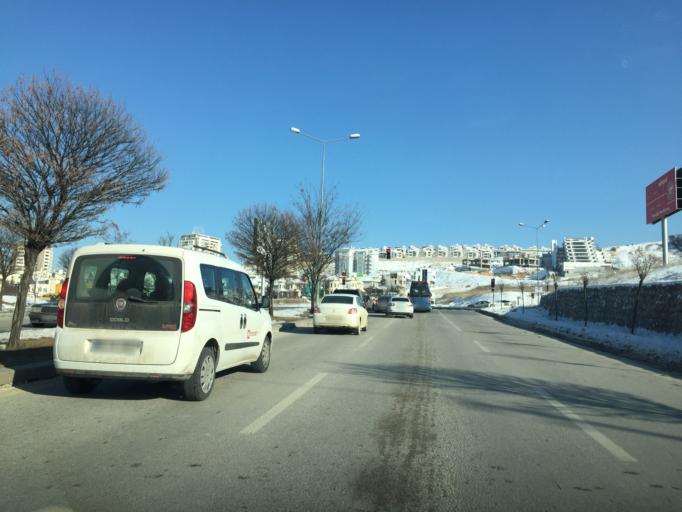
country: TR
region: Ankara
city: Batikent
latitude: 39.8850
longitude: 32.6984
